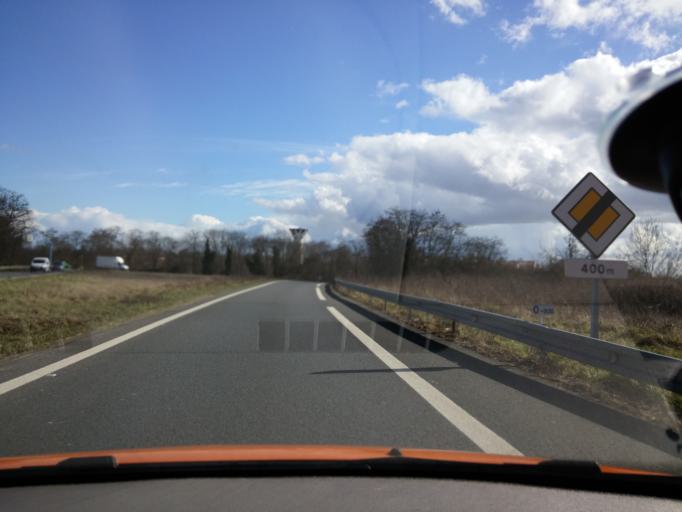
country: FR
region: Ile-de-France
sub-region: Departement de l'Essonne
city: Chilly-Mazarin
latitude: 48.7101
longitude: 2.3037
